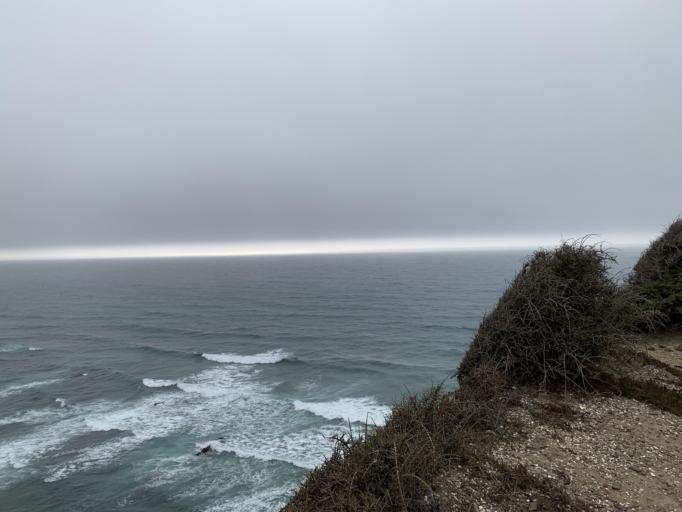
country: PT
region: Faro
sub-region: Aljezur
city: Aljezur
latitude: 37.3374
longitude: -8.8576
